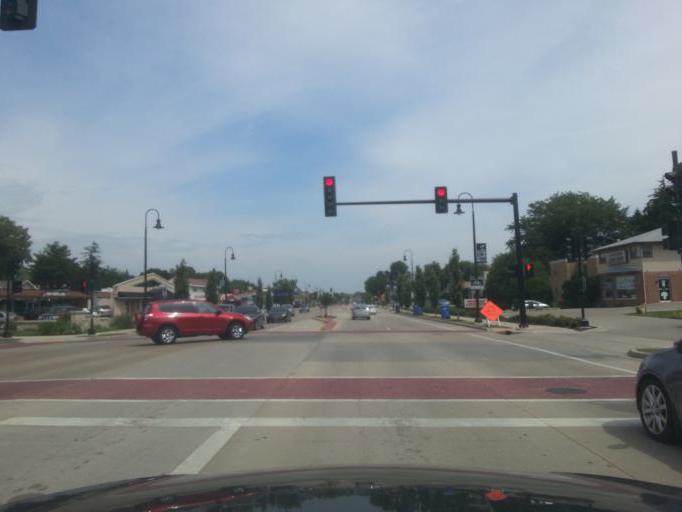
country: US
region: Wisconsin
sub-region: Dane County
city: Monona
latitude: 43.0569
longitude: -89.3256
